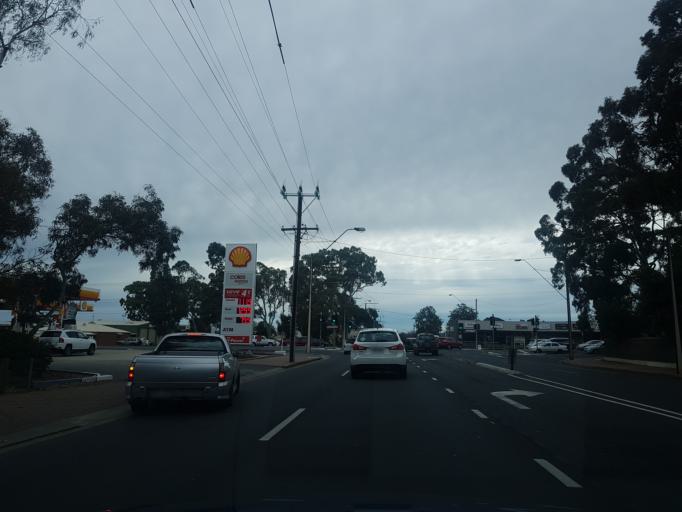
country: AU
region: South Australia
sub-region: Campbelltown
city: Campbelltown
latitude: -34.8893
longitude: 138.6742
